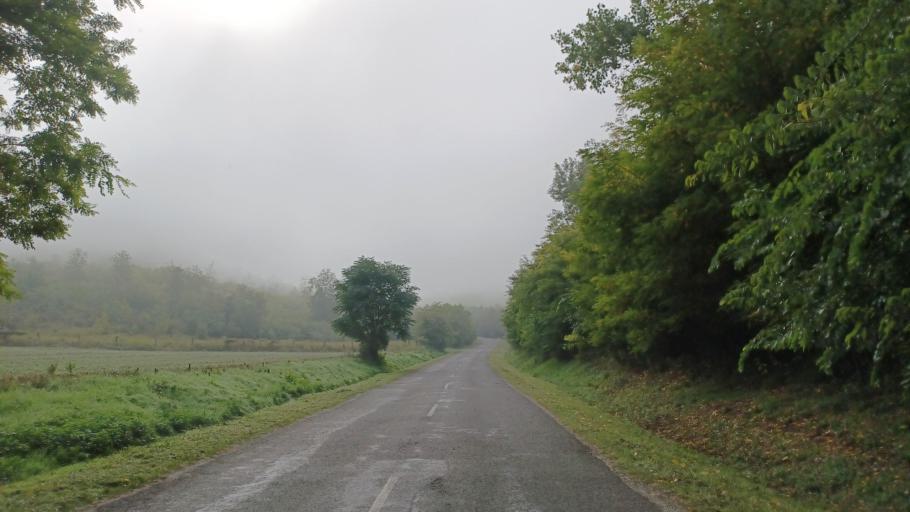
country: HU
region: Tolna
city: Pincehely
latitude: 46.6846
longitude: 18.4620
